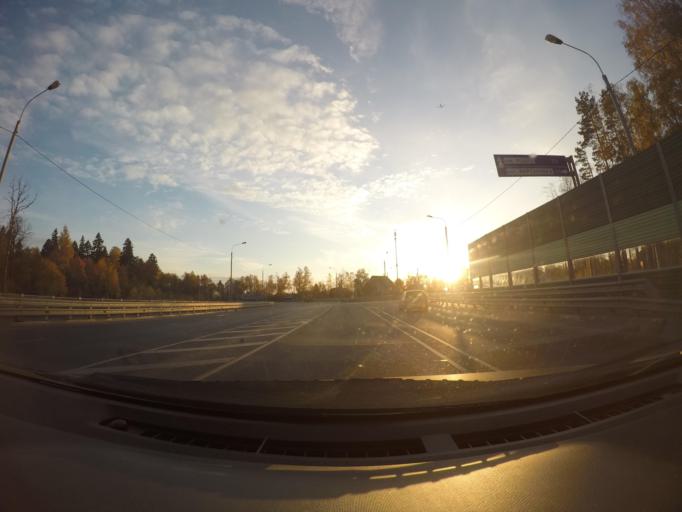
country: RU
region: Moskovskaya
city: Firsanovka
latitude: 55.9501
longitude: 37.2530
